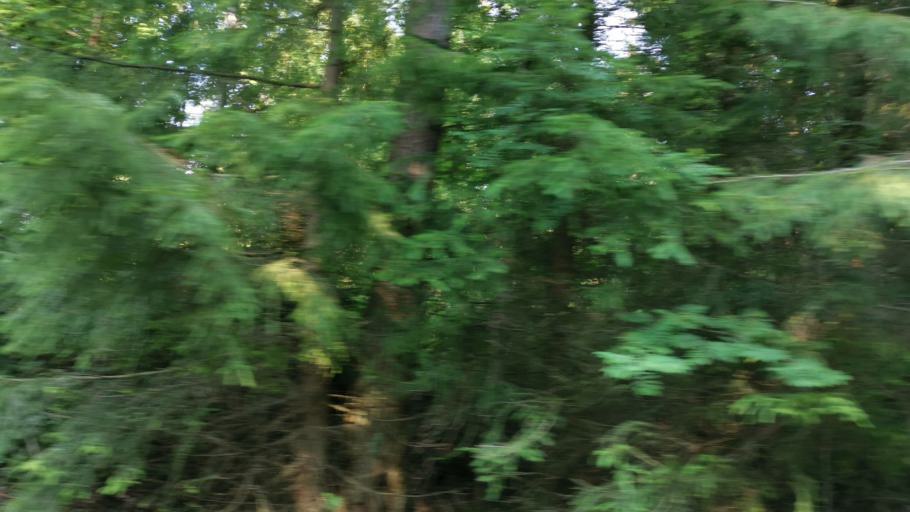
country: SE
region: Vaestra Goetaland
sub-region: Orust
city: Henan
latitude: 58.2911
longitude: 11.6475
